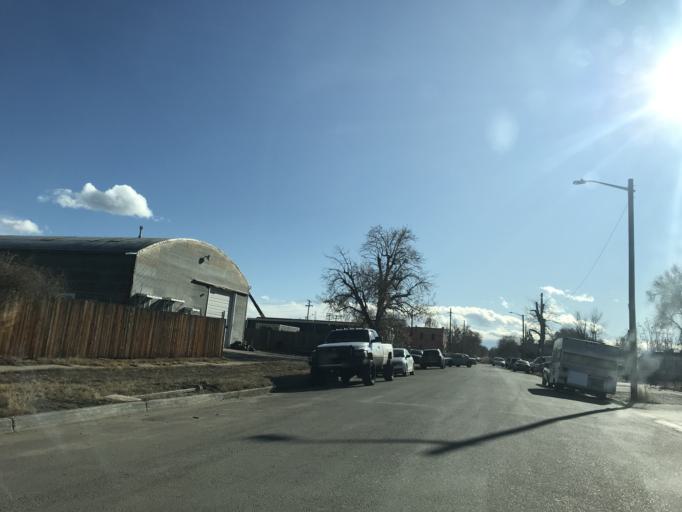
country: US
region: Colorado
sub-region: Denver County
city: Denver
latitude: 39.7728
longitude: -104.9647
